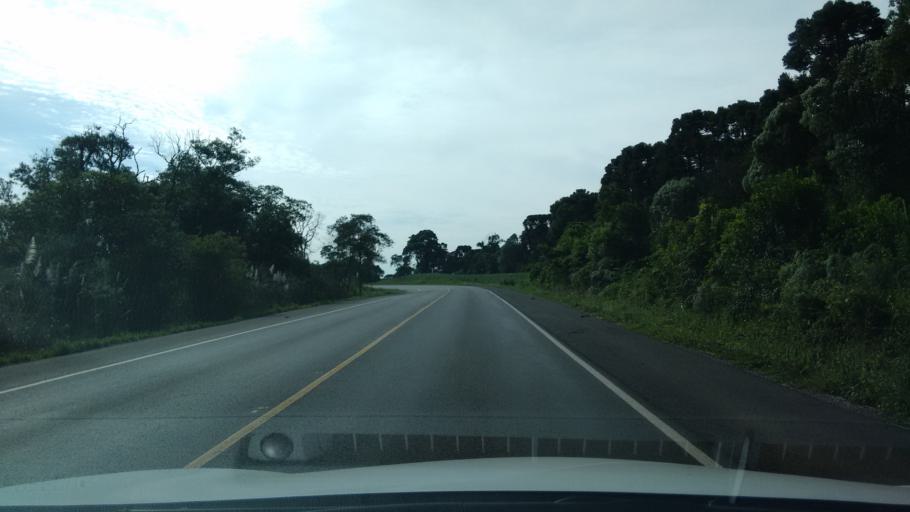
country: BR
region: Santa Catarina
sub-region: Campos Novos
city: Campos Novos
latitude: -27.3312
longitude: -50.9138
